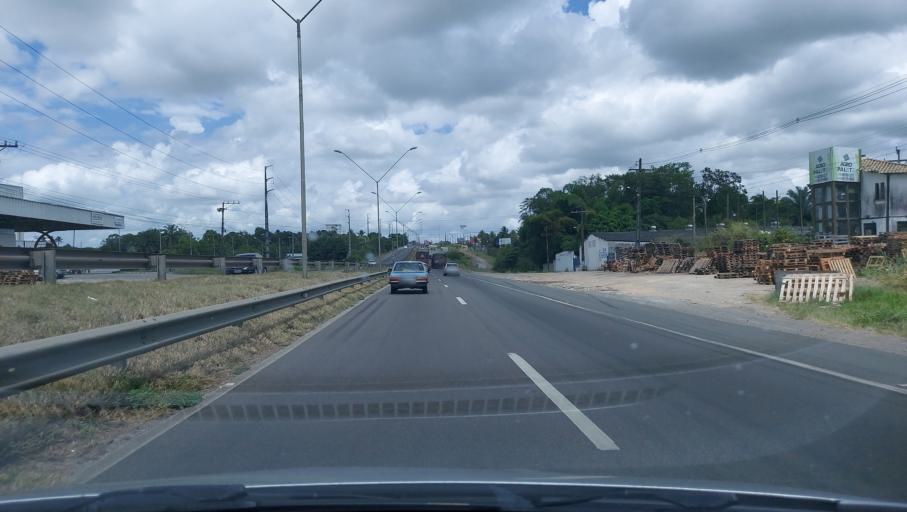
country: BR
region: Bahia
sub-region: Conceicao Do Jacuipe
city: Conceicao do Jacuipe
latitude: -12.3246
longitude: -38.8663
